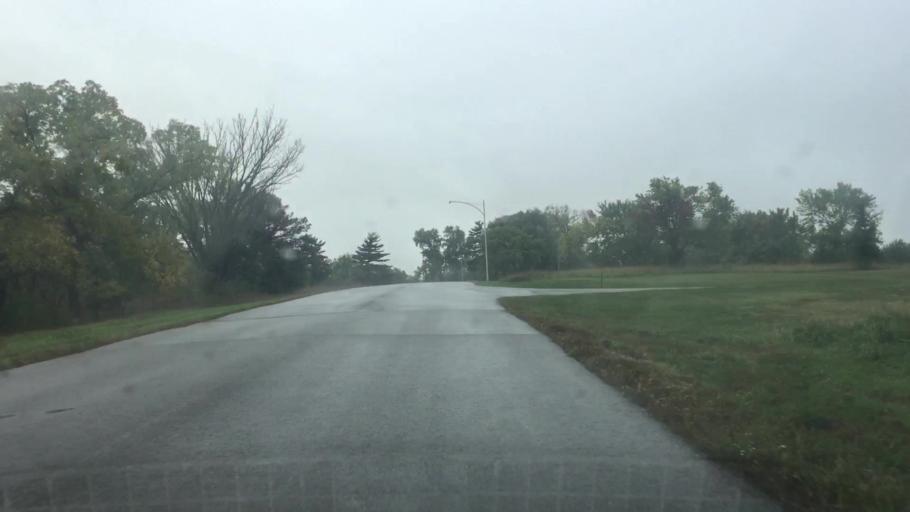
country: US
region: Kansas
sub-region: Johnson County
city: Lenexa
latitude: 38.9773
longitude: -94.8085
